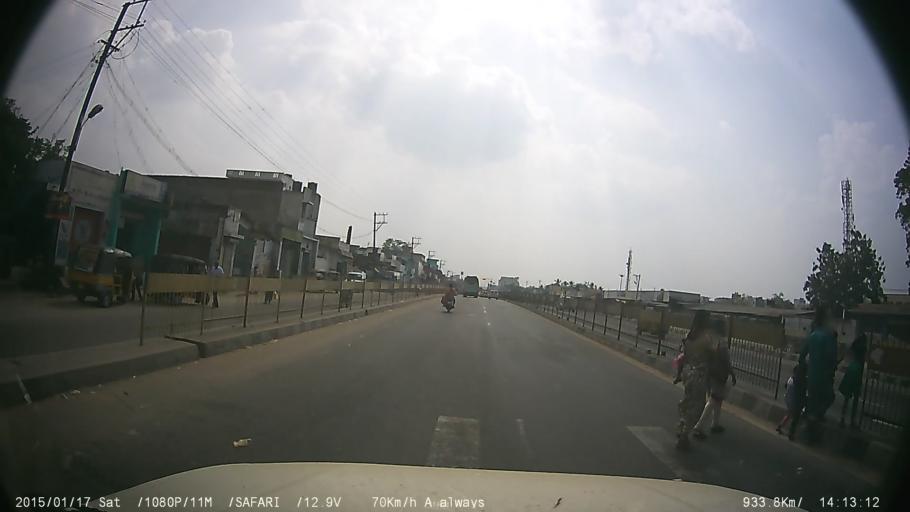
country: IN
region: Tamil Nadu
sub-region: Vellore
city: Ambur
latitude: 12.7820
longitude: 78.7192
